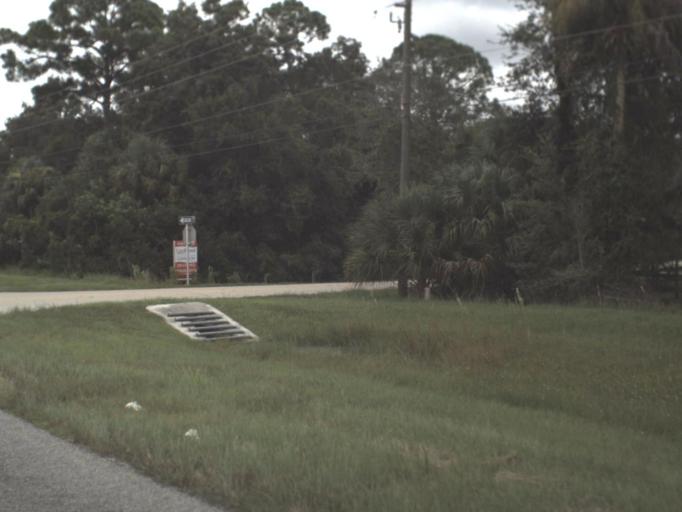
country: US
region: Florida
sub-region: Lee County
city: Alva
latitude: 26.7113
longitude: -81.6415
